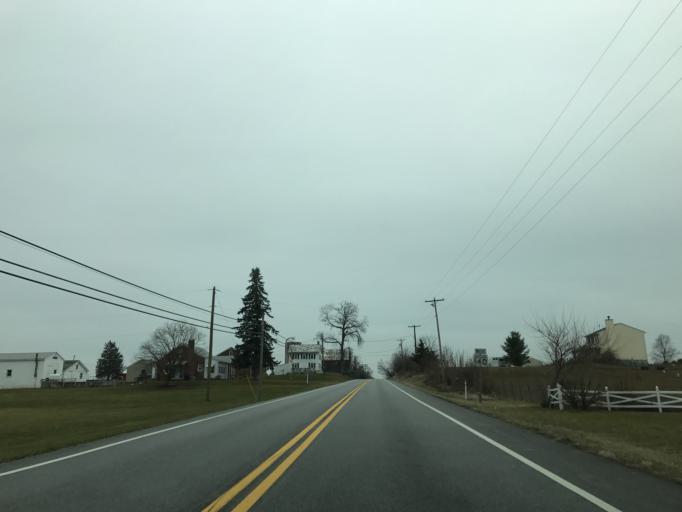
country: US
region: Maryland
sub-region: Carroll County
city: Taneytown
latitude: 39.6707
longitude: -77.2027
